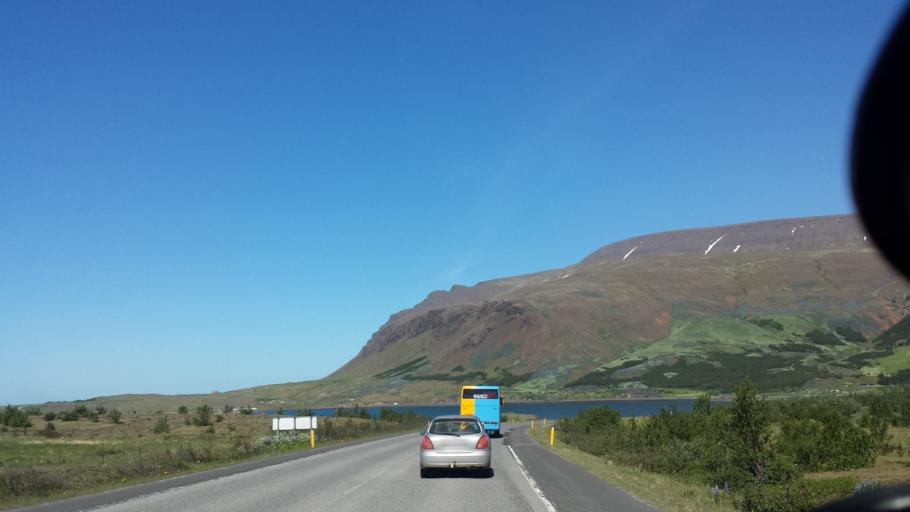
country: IS
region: Capital Region
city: Mosfellsbaer
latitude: 64.1971
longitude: -21.7043
